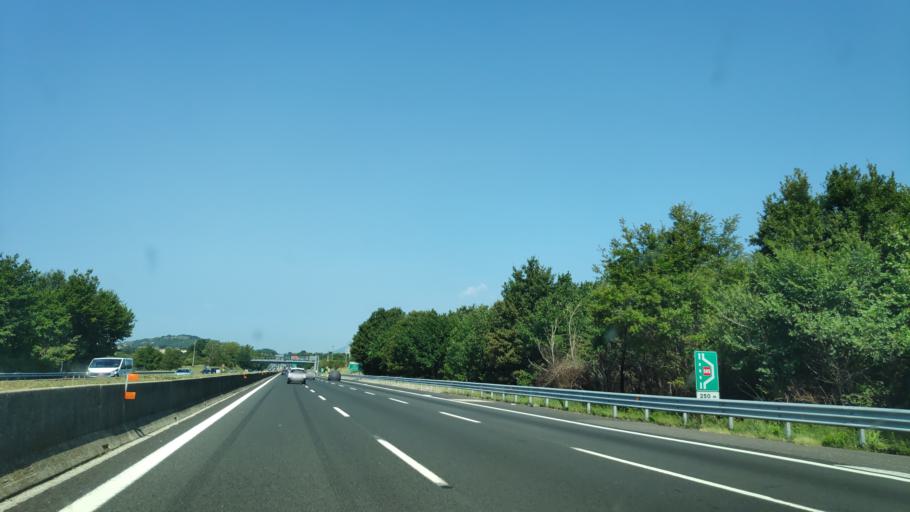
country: IT
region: Campania
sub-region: Provincia di Caserta
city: Bivio Mortola
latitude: 41.4248
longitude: 13.9184
